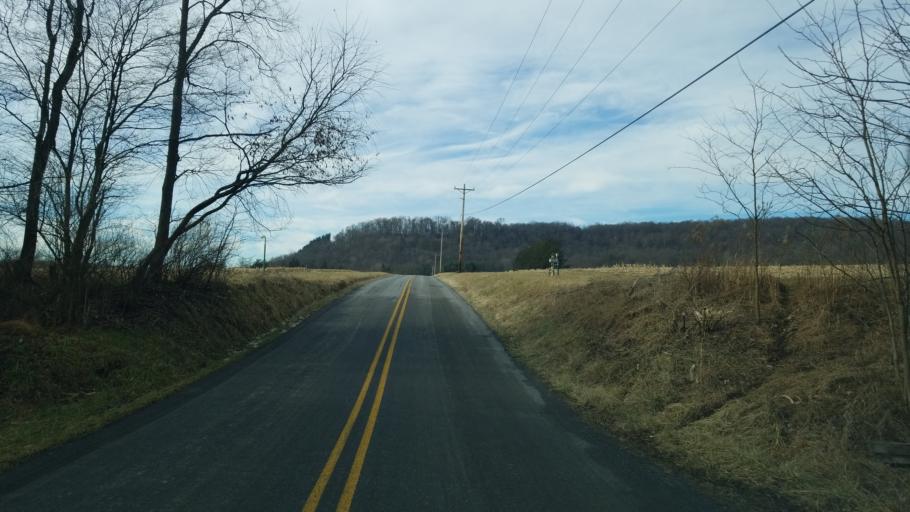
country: US
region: Pennsylvania
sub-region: Jefferson County
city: Punxsutawney
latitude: 40.8364
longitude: -79.1116
